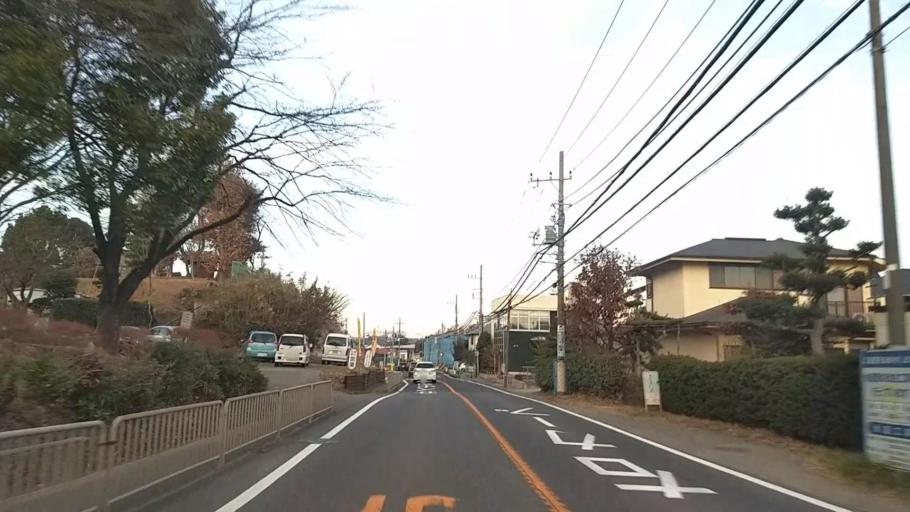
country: JP
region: Kanagawa
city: Atsugi
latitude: 35.4409
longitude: 139.3262
